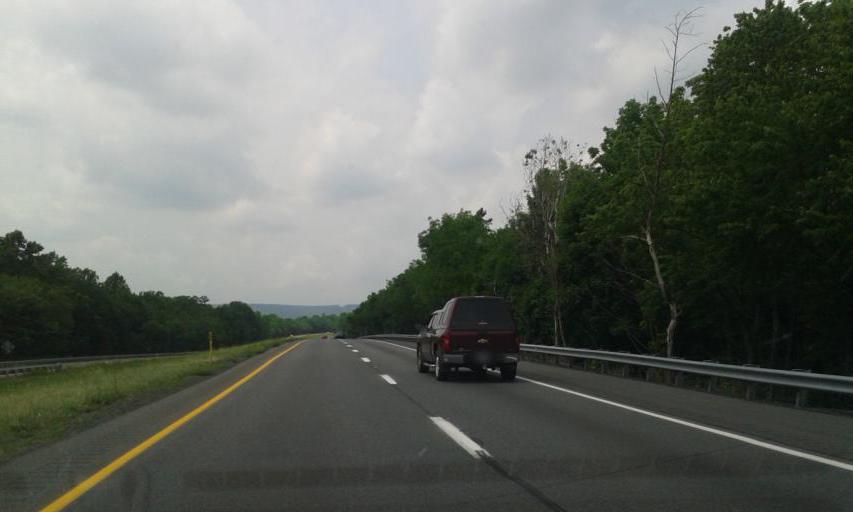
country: US
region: Pennsylvania
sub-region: Northampton County
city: Belfast
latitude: 40.7994
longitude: -75.2941
